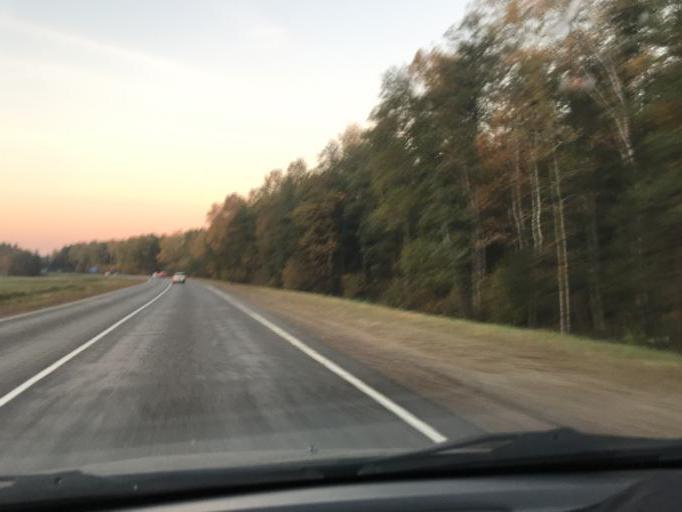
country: BY
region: Mogilev
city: Babruysk
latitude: 53.1996
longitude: 29.0639
